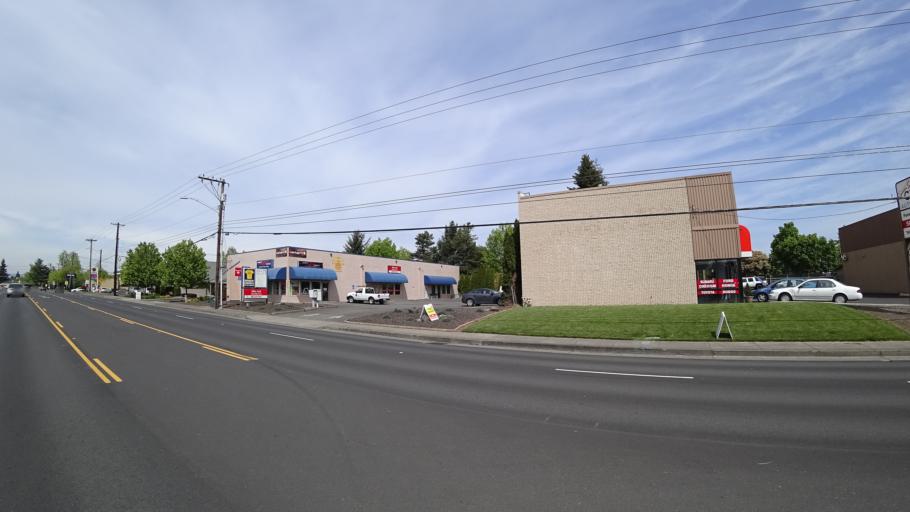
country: US
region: Oregon
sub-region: Washington County
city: Hillsboro
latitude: 45.5306
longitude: -122.9626
